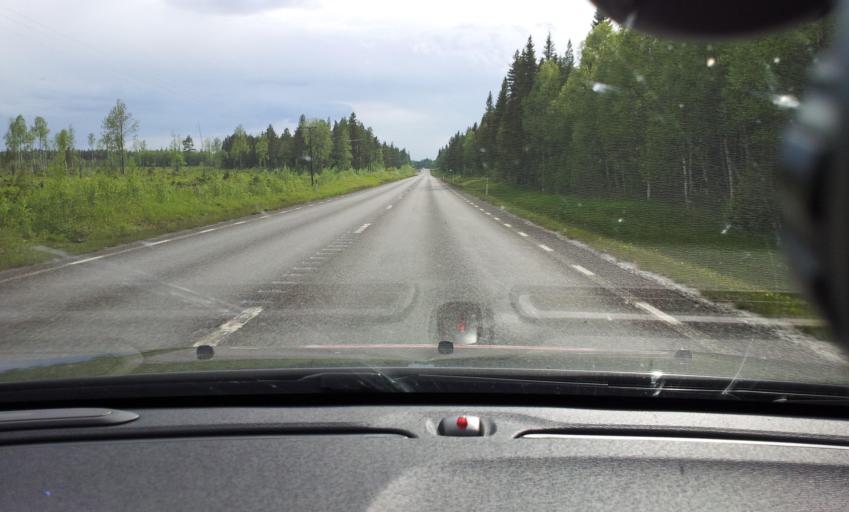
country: SE
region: Jaemtland
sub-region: OEstersunds Kommun
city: Lit
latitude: 63.2039
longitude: 14.8182
